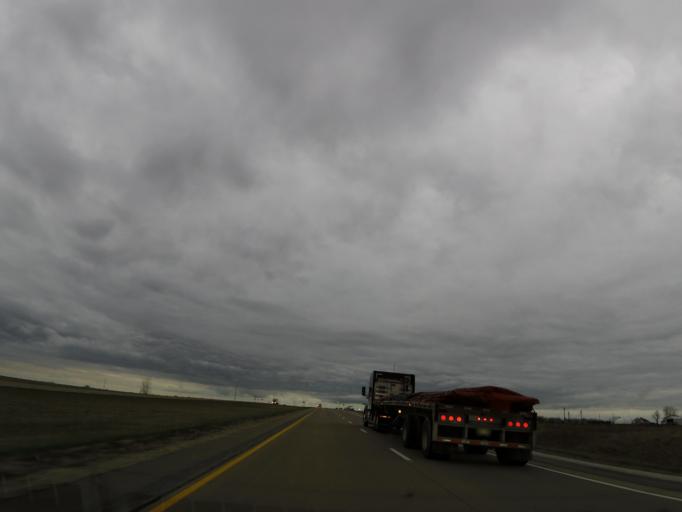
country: US
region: Iowa
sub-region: Henry County
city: Winfield
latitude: 41.1453
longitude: -91.5401
